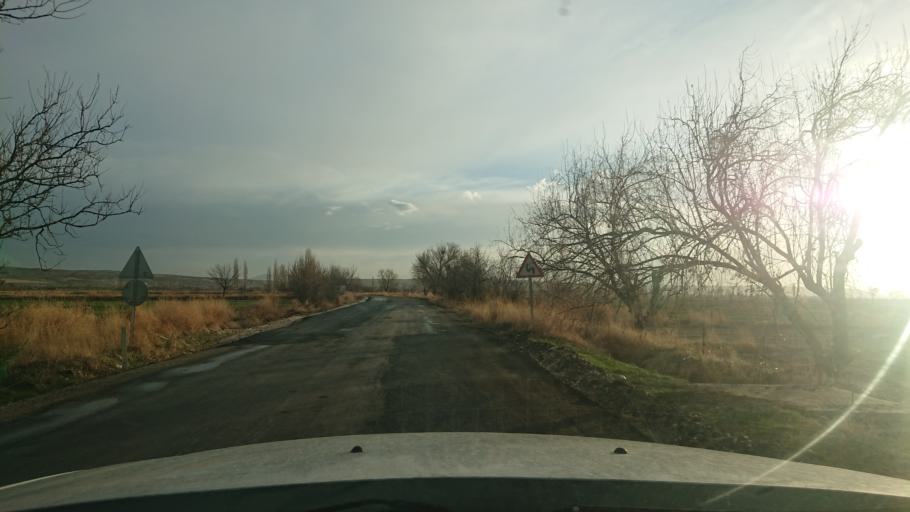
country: TR
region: Aksaray
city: Acipinar
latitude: 38.4763
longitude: 33.8736
